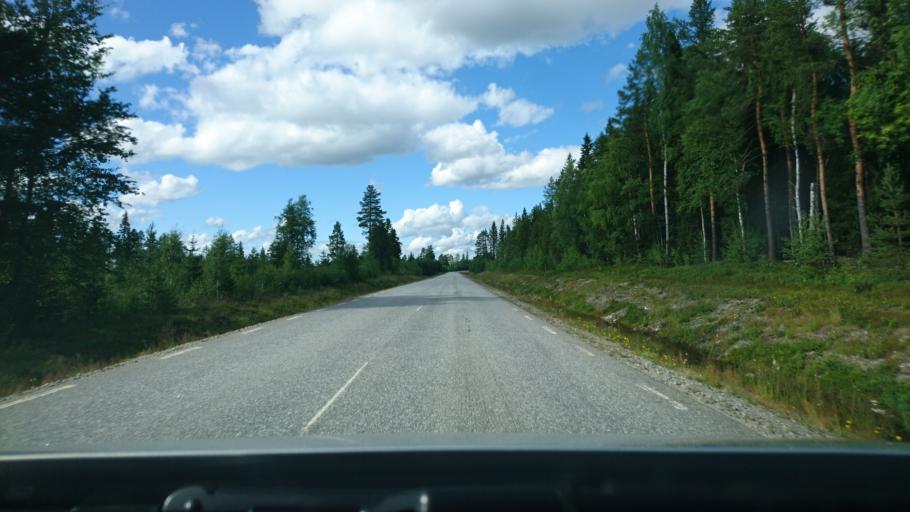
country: SE
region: Vaesterbotten
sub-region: Asele Kommun
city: Asele
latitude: 64.0527
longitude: 17.2809
